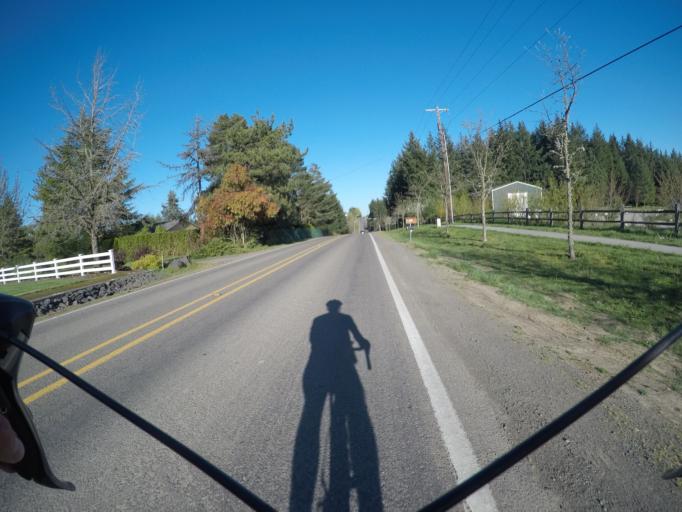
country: US
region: Oregon
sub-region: Washington County
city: Aloha
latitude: 45.4530
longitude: -122.8703
